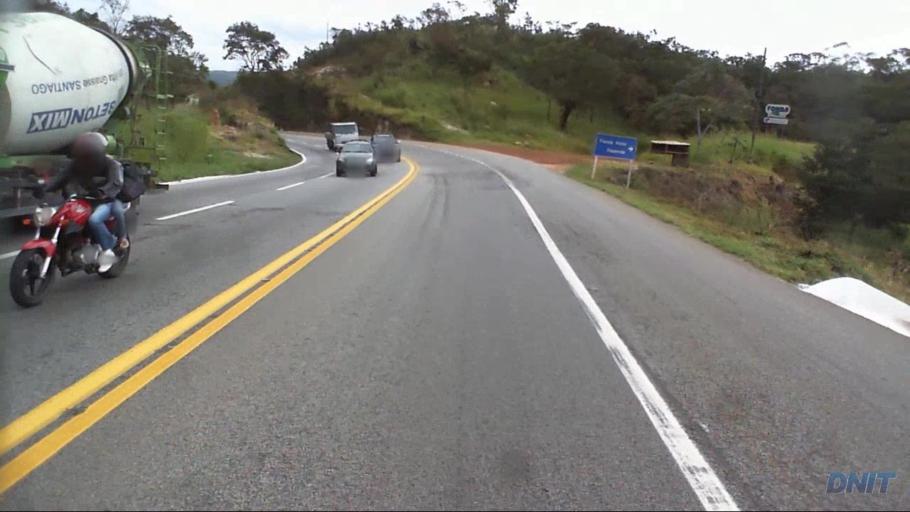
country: BR
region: Minas Gerais
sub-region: Caete
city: Caete
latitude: -19.7865
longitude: -43.7154
